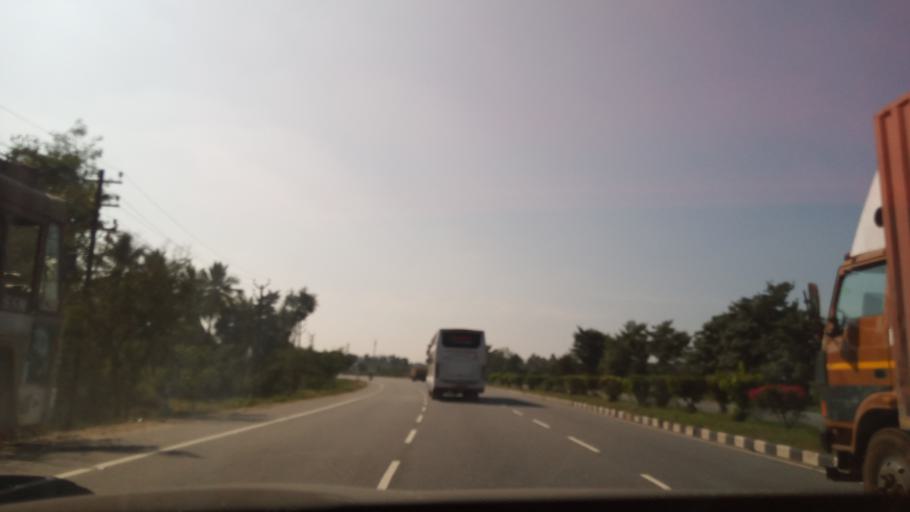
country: IN
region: Tamil Nadu
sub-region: Krishnagiri
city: Krishnagiri
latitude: 12.5343
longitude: 78.2952
